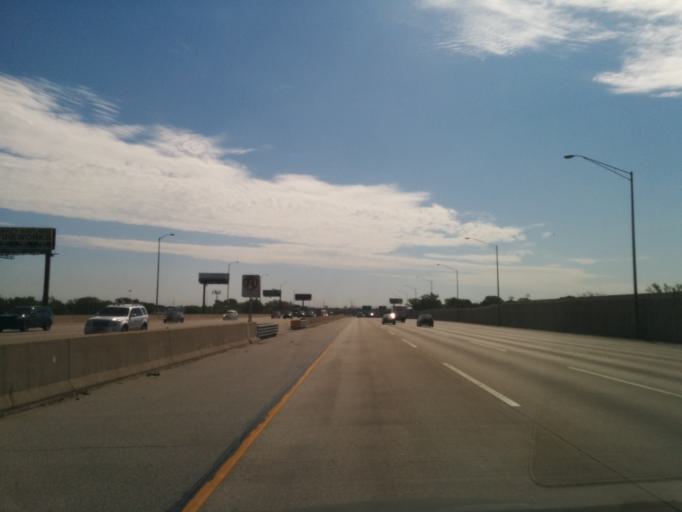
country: US
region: Illinois
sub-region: Cook County
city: East Hazel Crest
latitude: 41.5781
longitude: -87.6512
